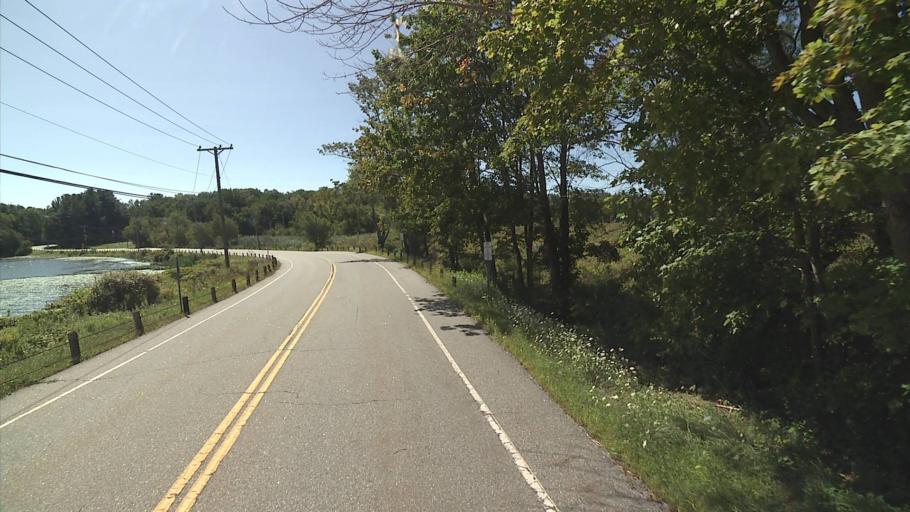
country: US
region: Connecticut
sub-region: Litchfield County
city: Bethlehem Village
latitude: 41.6882
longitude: -73.2323
